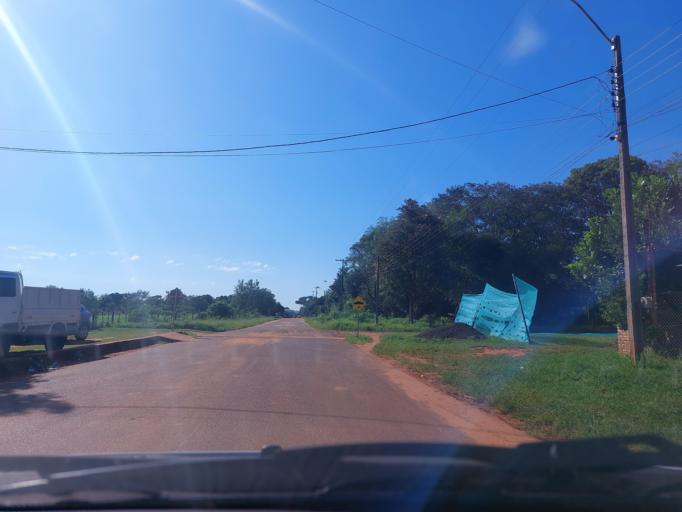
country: PY
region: San Pedro
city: Guayaybi
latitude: -24.5308
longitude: -56.4001
